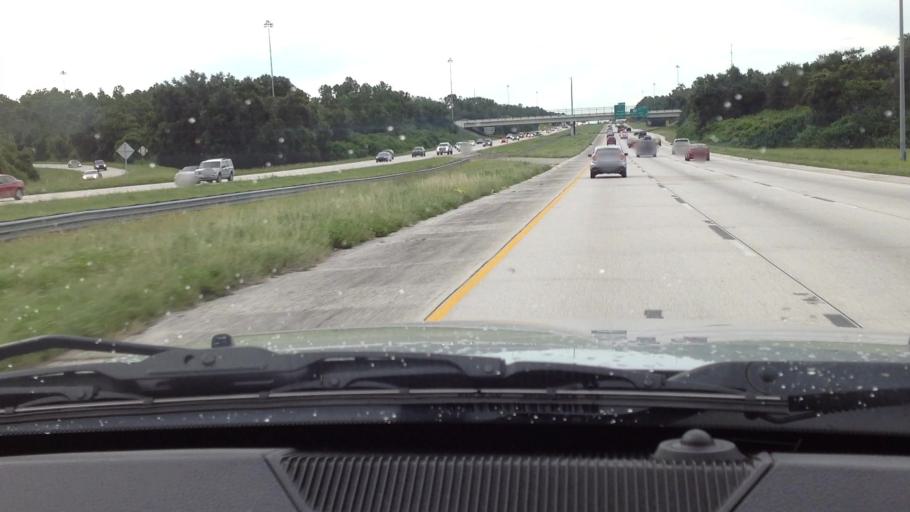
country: US
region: Florida
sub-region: Hillsborough County
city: Mango
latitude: 27.9734
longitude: -82.3243
